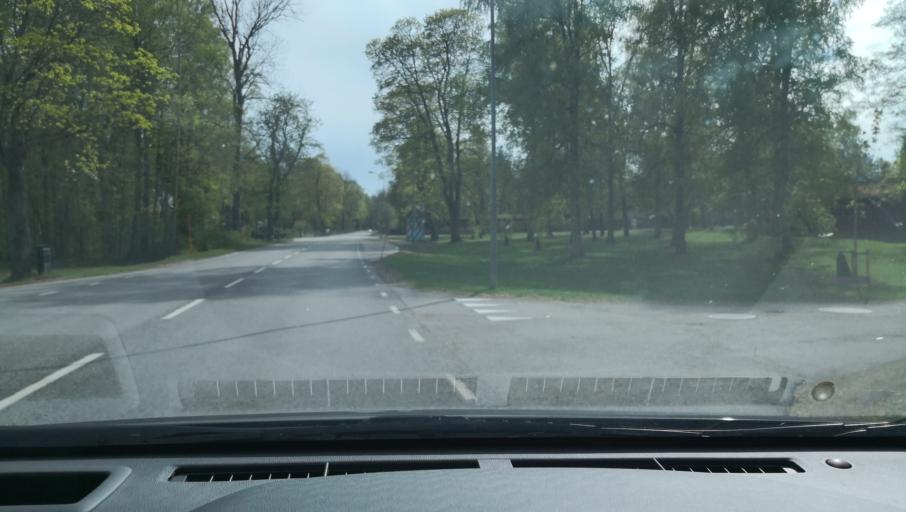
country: SE
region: OErebro
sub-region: Kumla Kommun
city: Kumla
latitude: 59.0963
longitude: 15.1616
